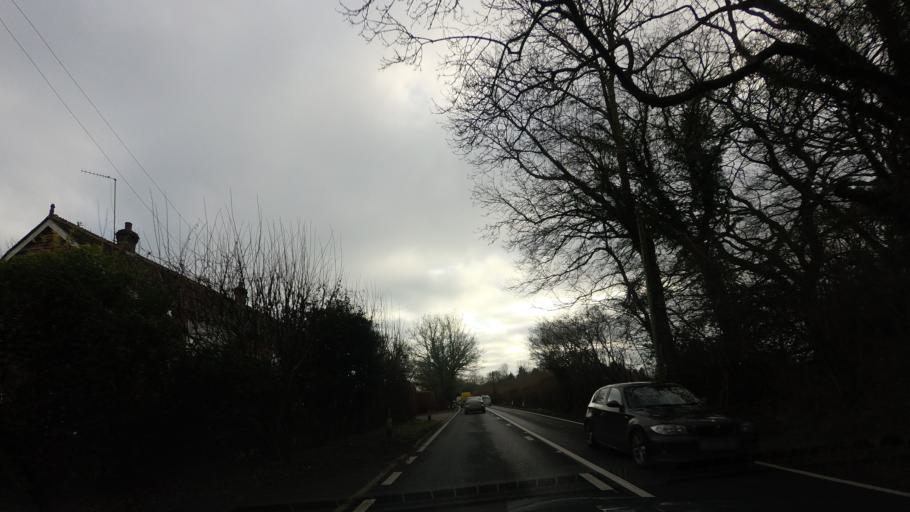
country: GB
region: England
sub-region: East Sussex
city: Wadhurst
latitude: 51.0750
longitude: 0.4209
